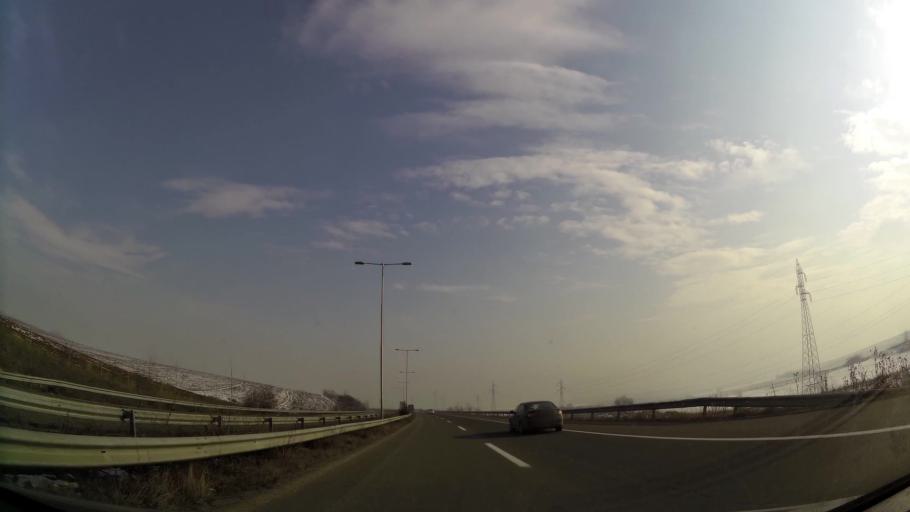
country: MK
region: Butel
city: Butel
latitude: 42.0335
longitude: 21.4739
